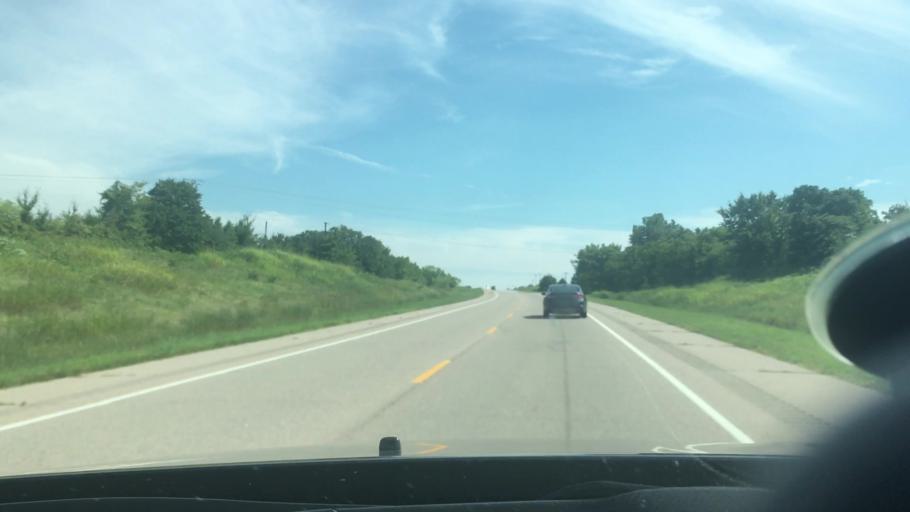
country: US
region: Oklahoma
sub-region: Seminole County
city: Konawa
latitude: 35.0490
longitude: -96.6807
